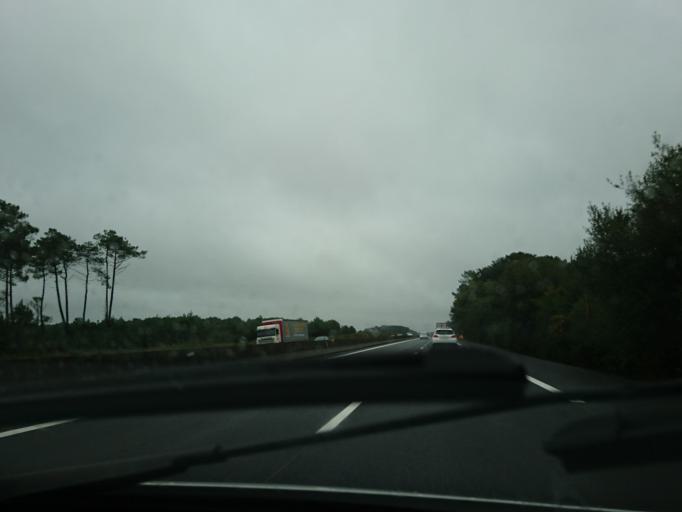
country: FR
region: Brittany
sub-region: Departement du Morbihan
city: Ploeren
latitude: 47.6634
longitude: -2.8889
